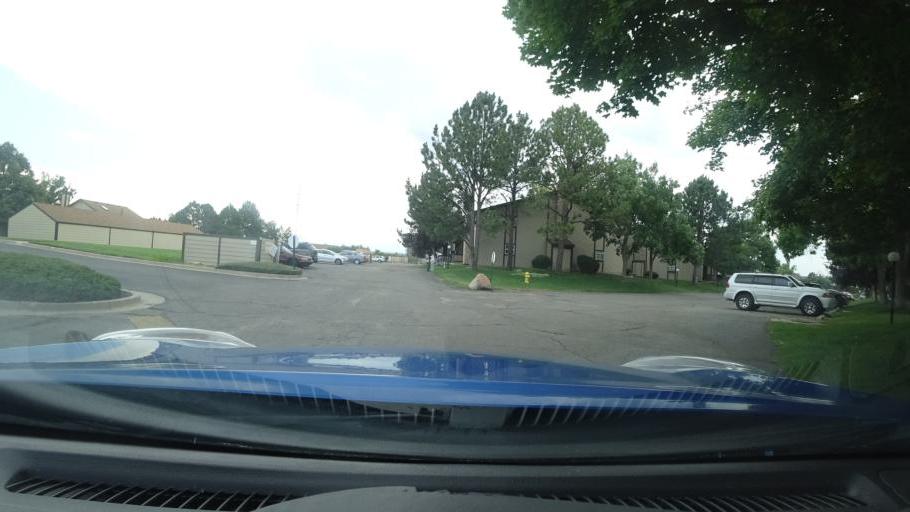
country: US
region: Colorado
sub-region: Adams County
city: Aurora
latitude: 39.6835
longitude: -104.7866
